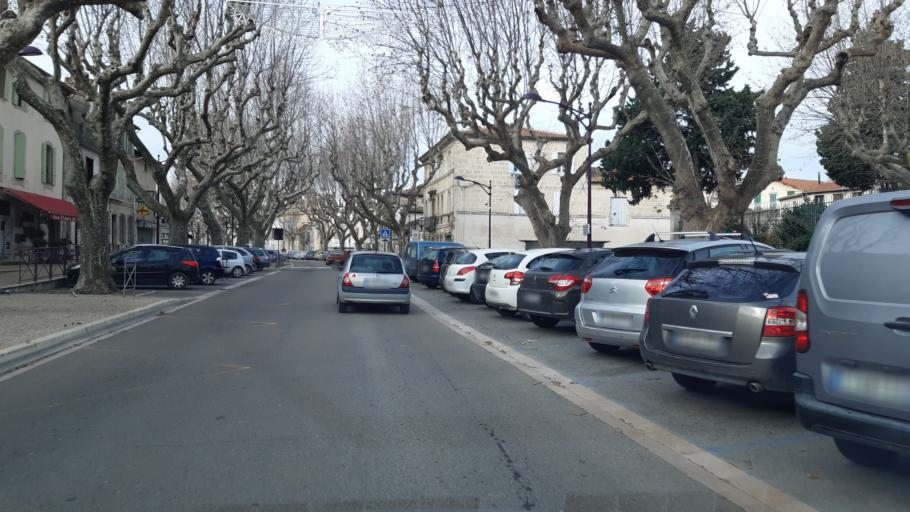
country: FR
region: Provence-Alpes-Cote d'Azur
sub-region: Departement des Bouches-du-Rhone
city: Tarascon
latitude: 43.8029
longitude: 4.6620
